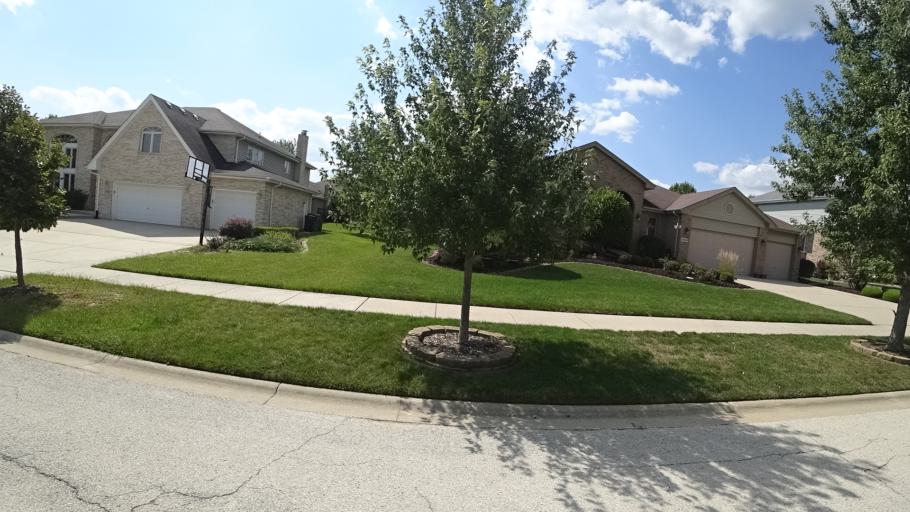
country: US
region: Illinois
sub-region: Cook County
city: Palos Heights
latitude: 41.6336
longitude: -87.8106
